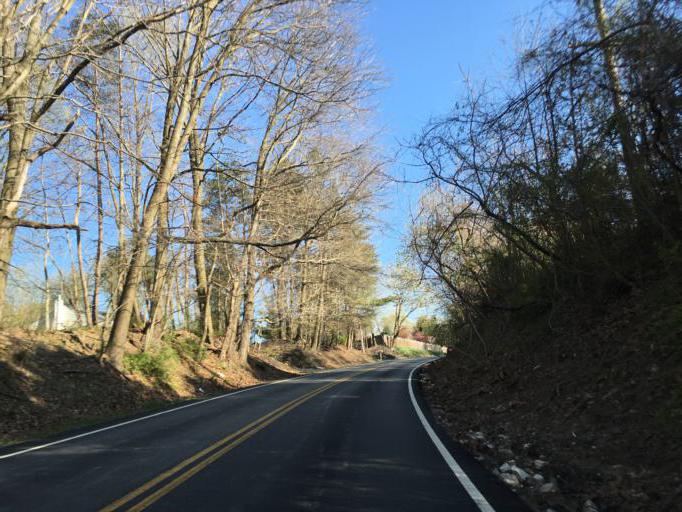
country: US
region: Maryland
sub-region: Baltimore County
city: Hampton
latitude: 39.5023
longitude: -76.5307
